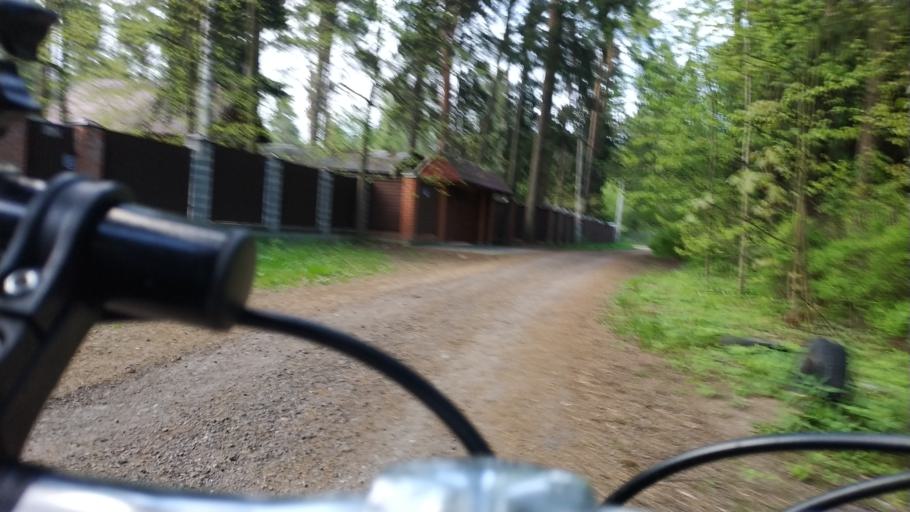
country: RU
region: Moskovskaya
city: Kratovo
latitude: 55.6019
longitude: 38.1560
